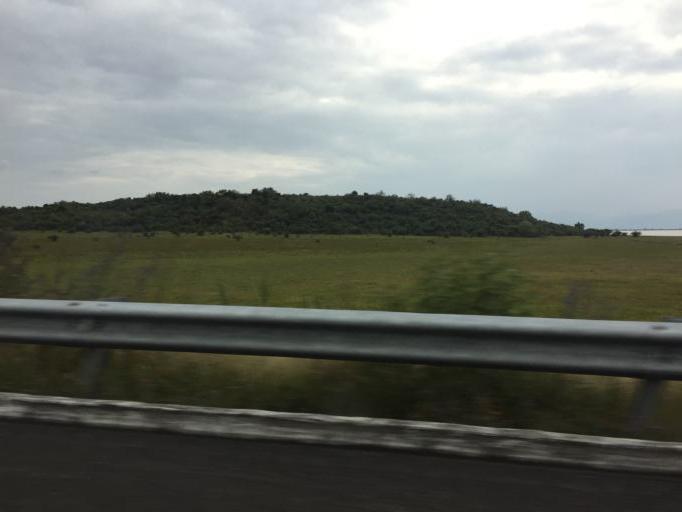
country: MX
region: Michoacan
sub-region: Puruandiro
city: San Lorenzo
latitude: 19.9447
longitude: -101.6345
